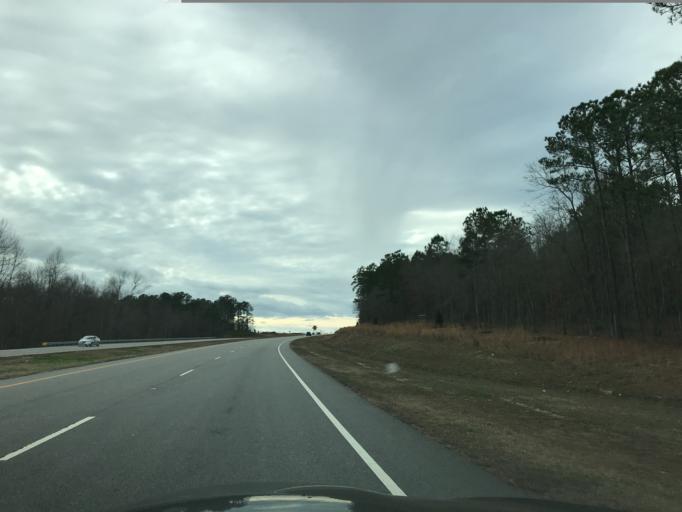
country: US
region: North Carolina
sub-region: Wake County
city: Rolesville
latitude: 35.9193
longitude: -78.4440
